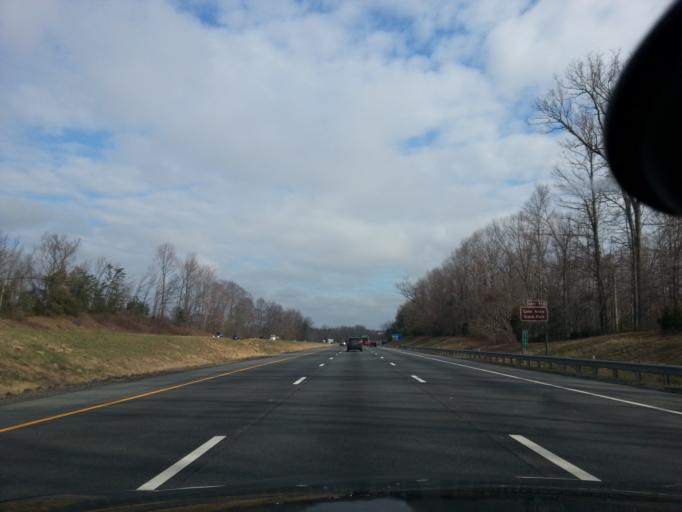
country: US
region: Virginia
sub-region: Spotsylvania County
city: Spotsylvania Courthouse
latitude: 38.1091
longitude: -77.5178
